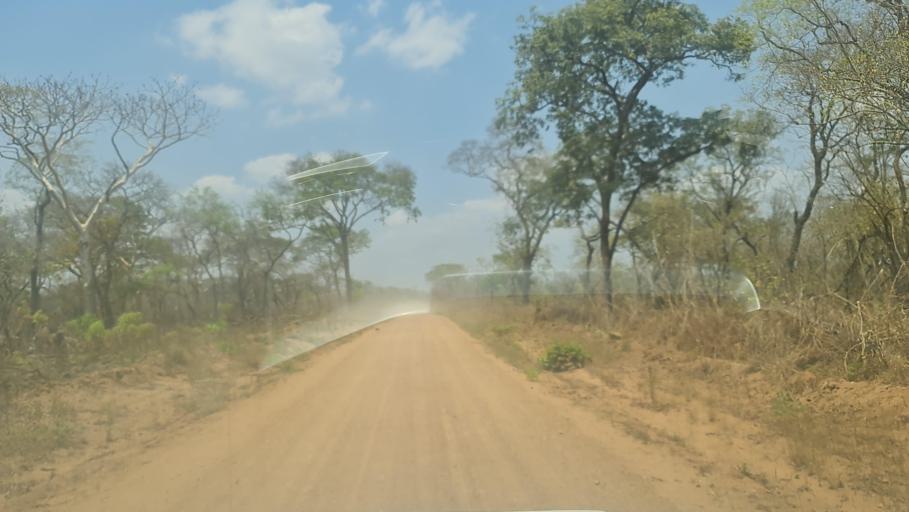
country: MW
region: Southern Region
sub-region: Nsanje District
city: Nsanje
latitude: -17.5601
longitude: 35.8993
